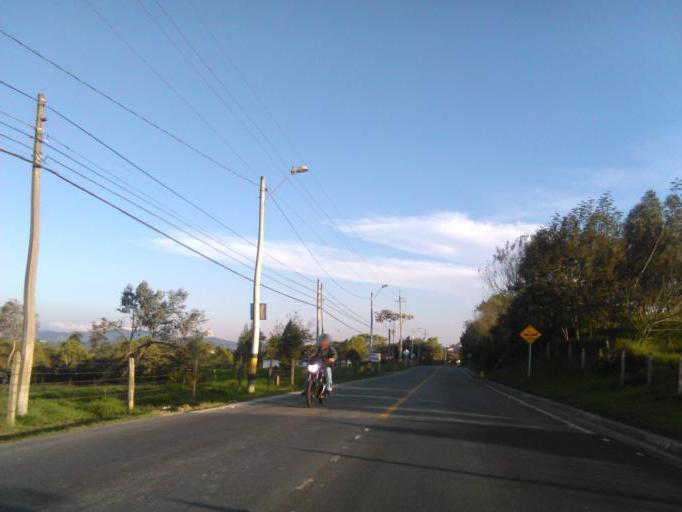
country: CO
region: Antioquia
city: La Union
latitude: 5.9883
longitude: -75.3724
